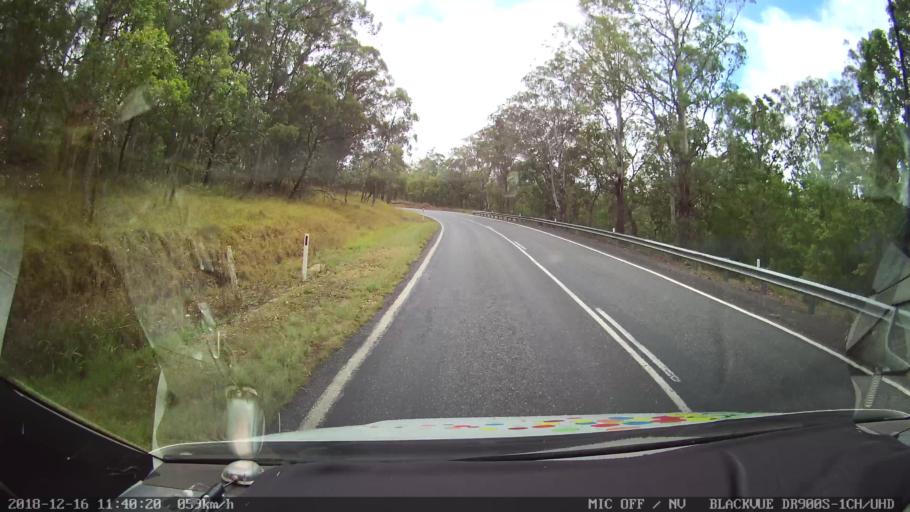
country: AU
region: New South Wales
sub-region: Tenterfield Municipality
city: Carrolls Creek
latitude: -28.9616
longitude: 152.1980
